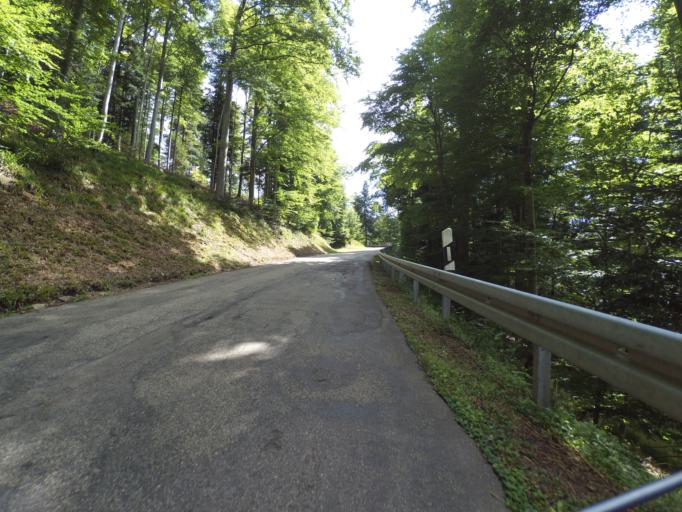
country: DE
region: Baden-Wuerttemberg
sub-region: Freiburg Region
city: Waldkirch
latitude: 48.0764
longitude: 8.0001
